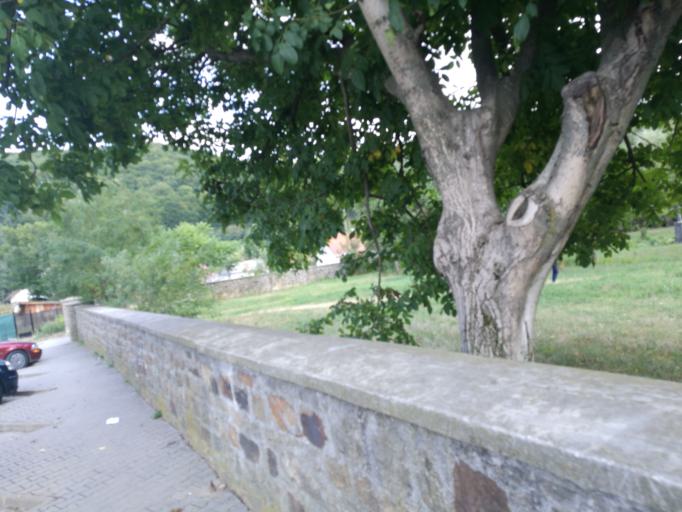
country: RO
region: Suceava
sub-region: Comuna Patrauti
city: Patrauti
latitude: 47.7297
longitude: 26.1928
